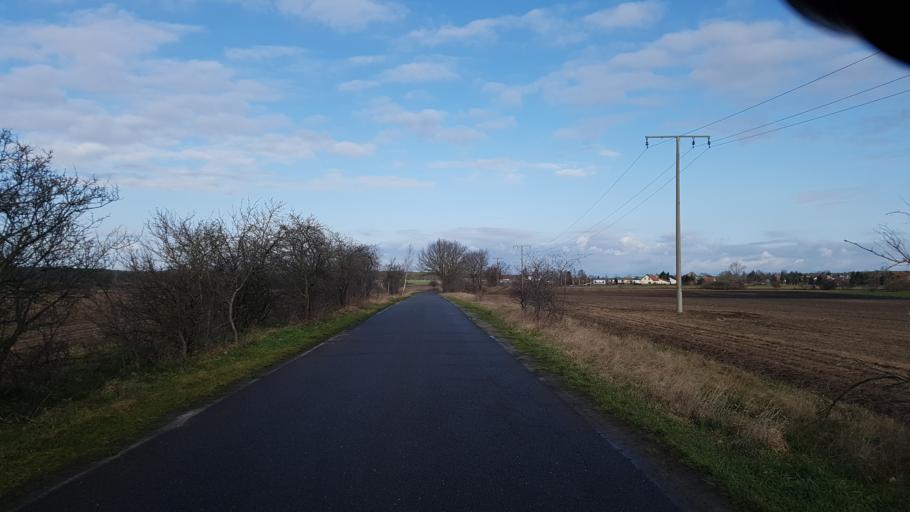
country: DE
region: Brandenburg
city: Schlieben
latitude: 51.7162
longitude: 13.3123
